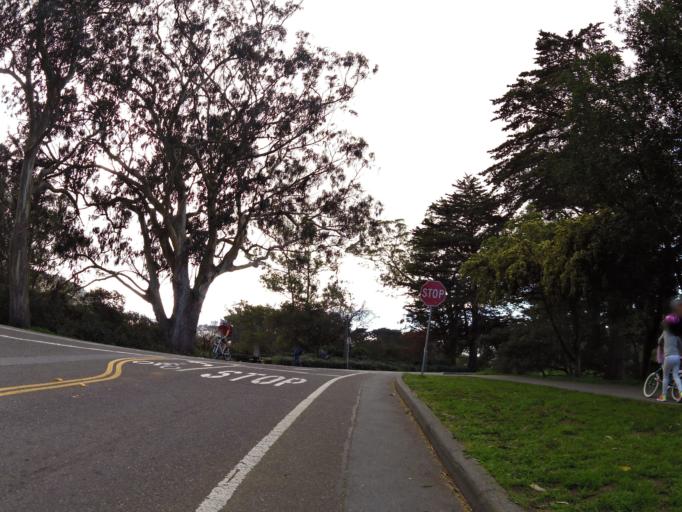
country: US
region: California
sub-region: San Francisco County
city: San Francisco
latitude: 37.7735
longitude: -122.4590
